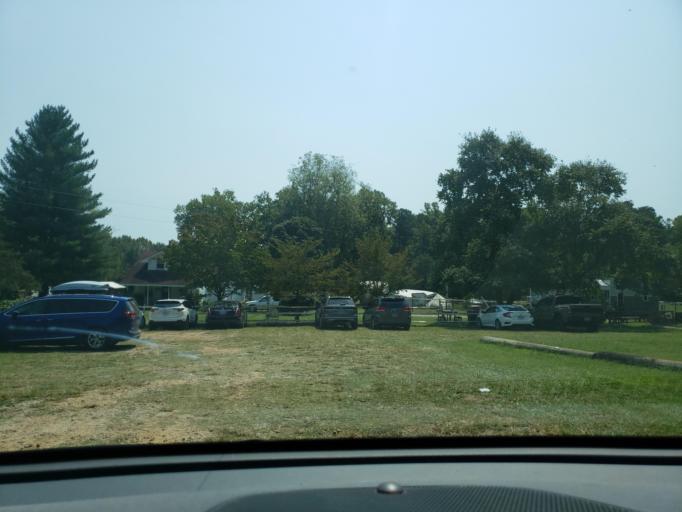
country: US
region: North Carolina
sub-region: Orange County
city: Hillsborough
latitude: 36.0042
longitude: -79.0845
